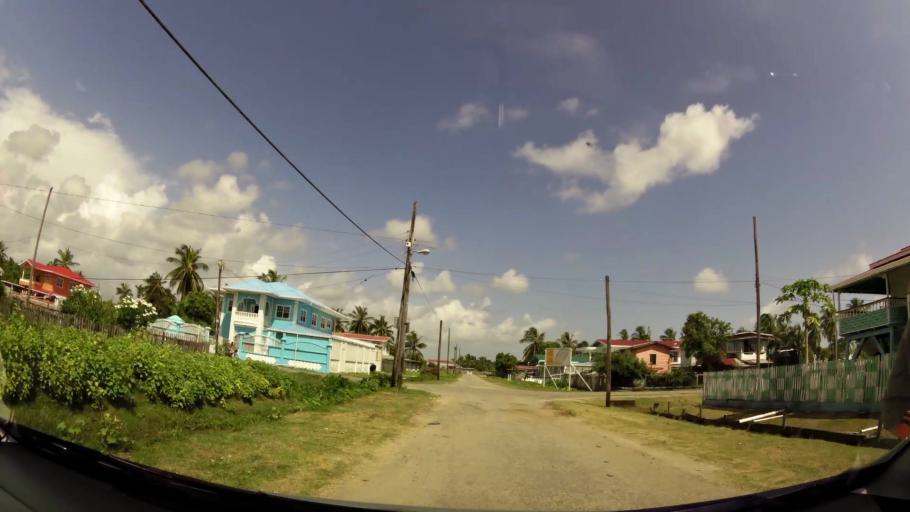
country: GY
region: Demerara-Mahaica
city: Mahaica Village
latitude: 6.7524
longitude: -57.9950
